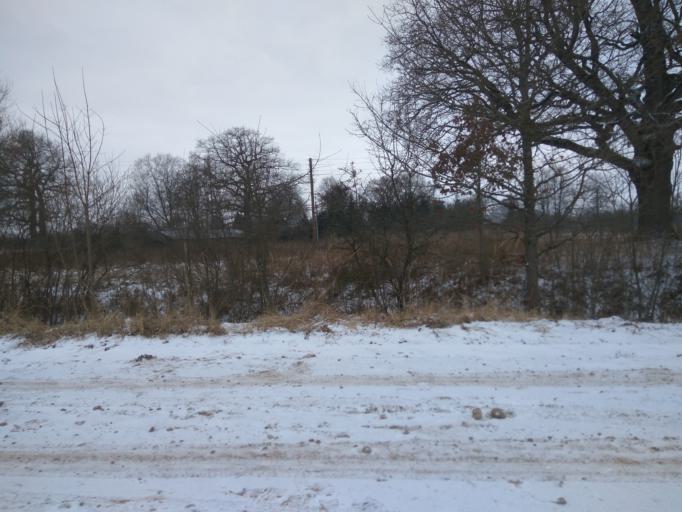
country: LV
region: Aizpute
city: Aizpute
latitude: 56.7140
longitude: 21.6383
